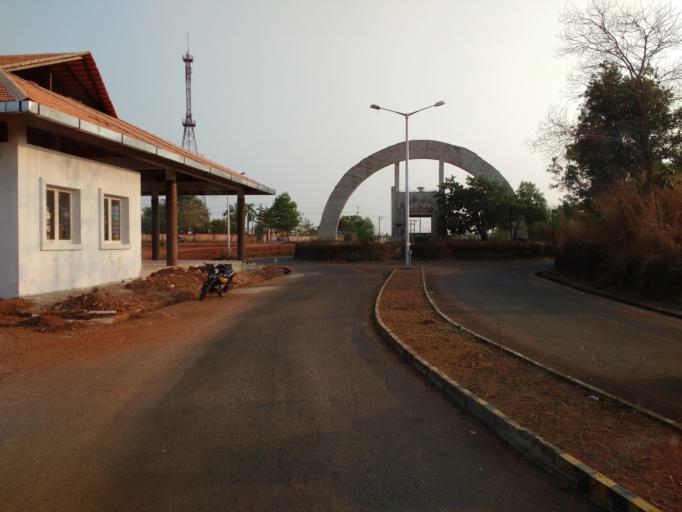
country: IN
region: Karnataka
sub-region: Dakshina Kannada
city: Mangalore
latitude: 12.9250
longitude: 74.9001
